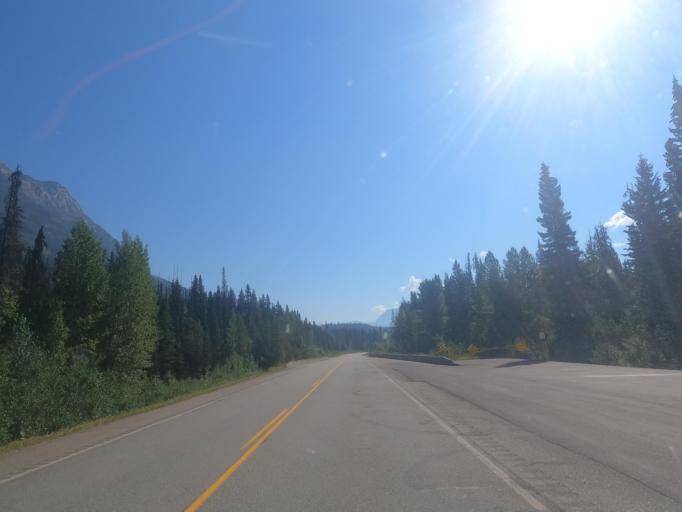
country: CA
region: Alberta
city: Jasper Park Lodge
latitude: 52.8629
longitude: -118.6503
